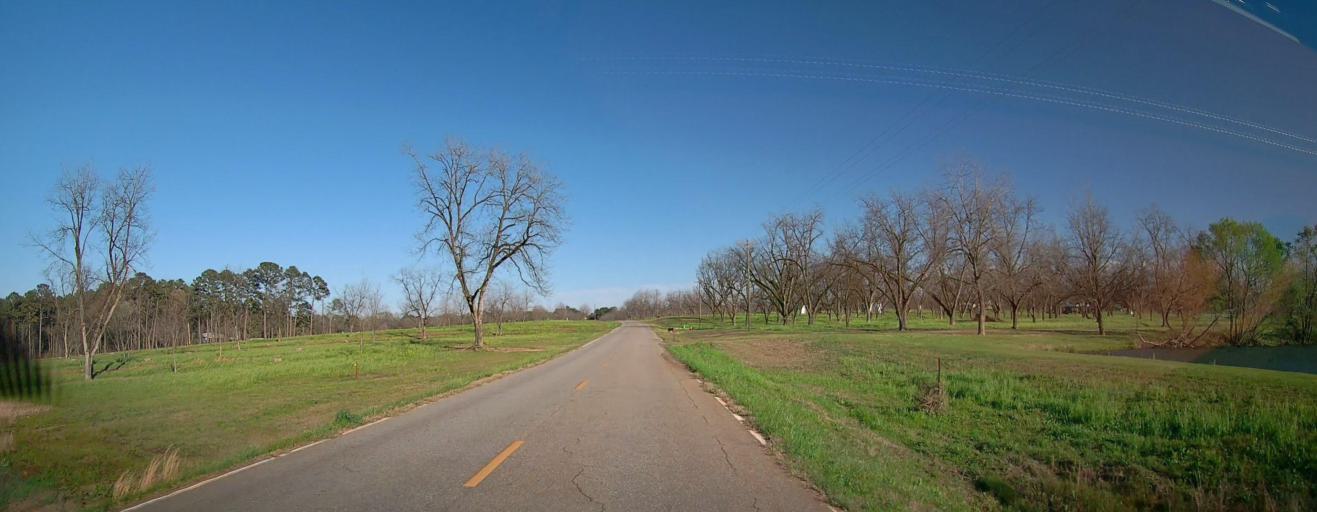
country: US
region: Georgia
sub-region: Houston County
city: Perry
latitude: 32.3666
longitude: -83.6808
